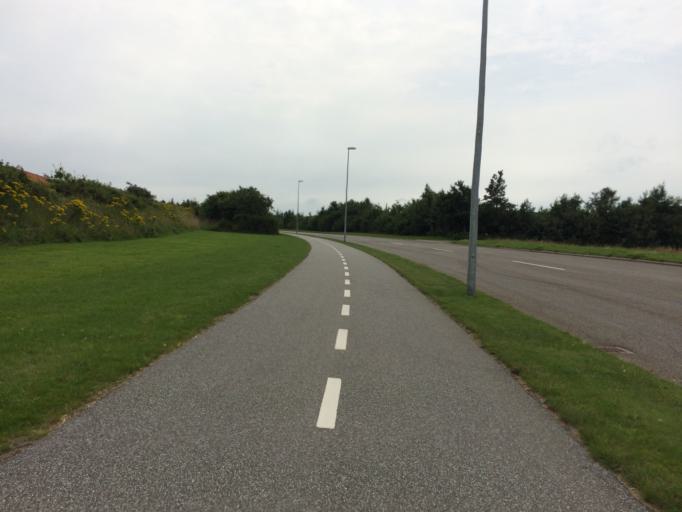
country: DK
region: Central Jutland
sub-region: Holstebro Kommune
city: Ulfborg
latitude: 56.2757
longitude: 8.3063
